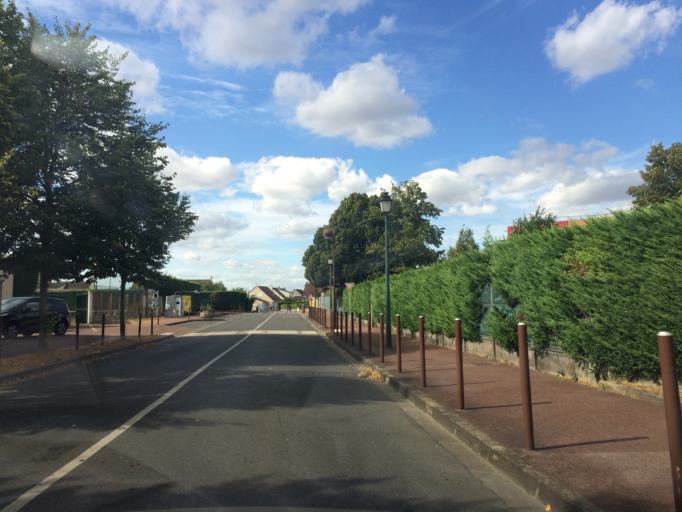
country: FR
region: Ile-de-France
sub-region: Departement de l'Essonne
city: Le Plessis-Pate
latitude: 48.6099
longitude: 2.3234
